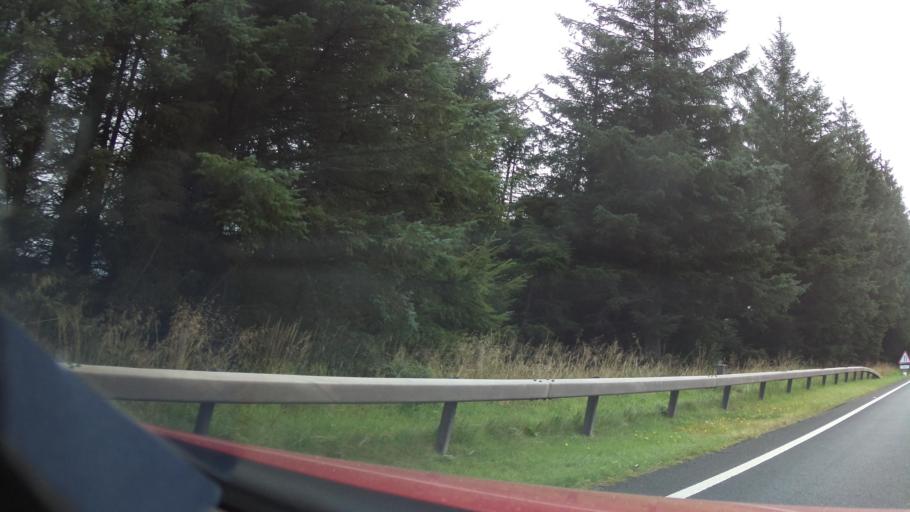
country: GB
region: Scotland
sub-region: East Lothian
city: Pencaitland
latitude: 55.8082
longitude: -2.8377
